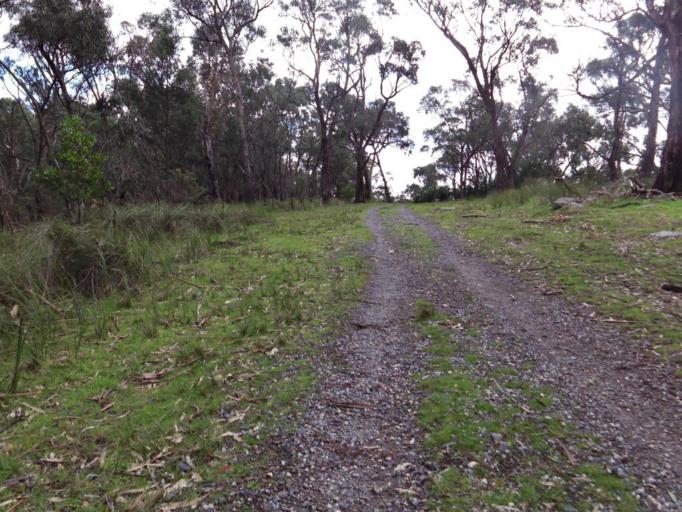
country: AU
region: Victoria
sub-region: Yarra Ranges
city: Lysterfield
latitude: -37.9341
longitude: 145.2900
